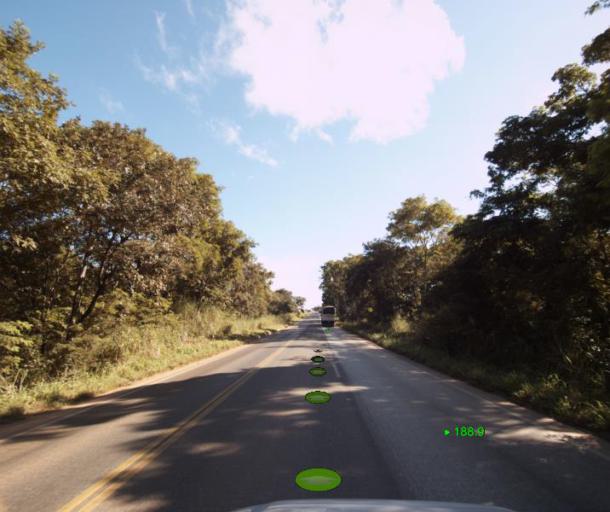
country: BR
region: Goias
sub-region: Uruacu
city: Uruacu
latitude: -14.5693
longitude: -49.1563
